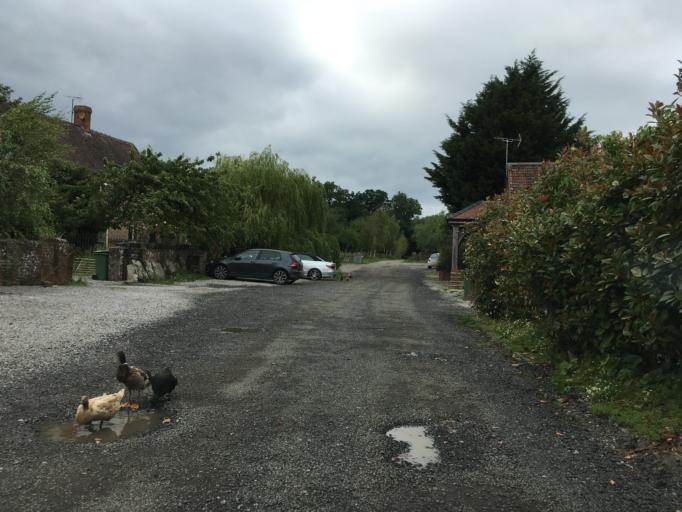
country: GB
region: England
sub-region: Gloucestershire
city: Cinderford
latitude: 51.7962
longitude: -2.4094
